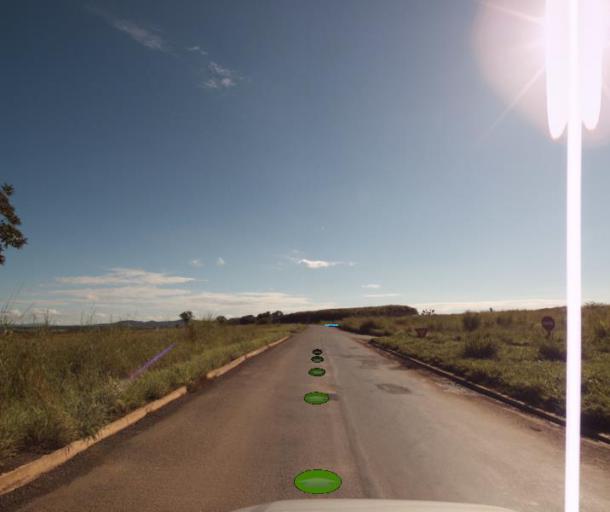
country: BR
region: Goias
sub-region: Uruacu
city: Uruacu
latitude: -14.6349
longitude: -49.1763
